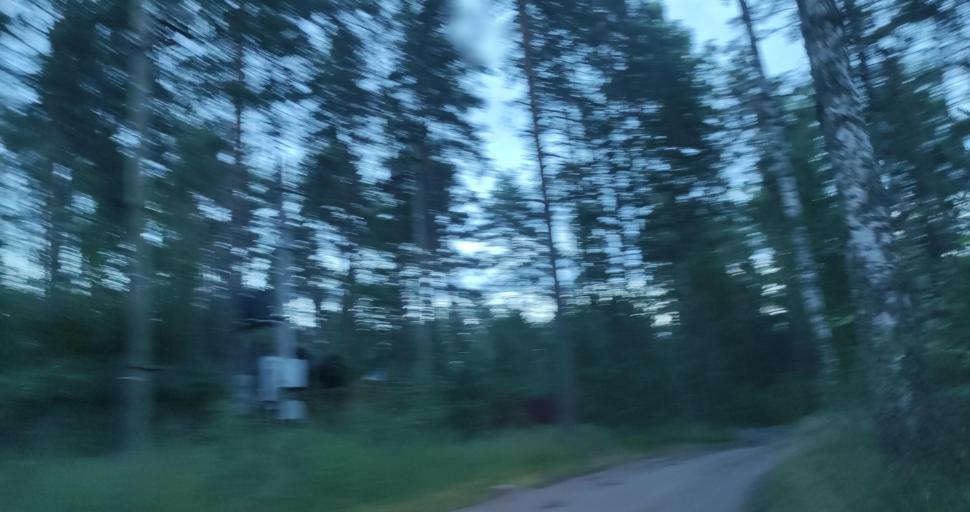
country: RU
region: Leningrad
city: Sapernoye
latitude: 60.6818
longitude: 29.9801
